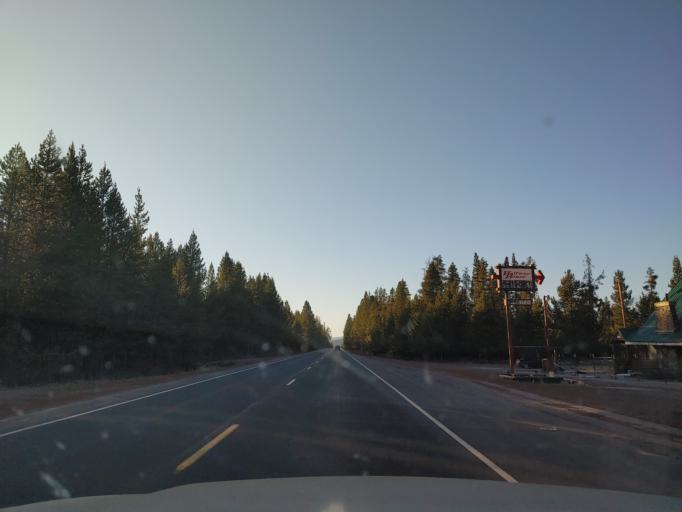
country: US
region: Oregon
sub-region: Deschutes County
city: La Pine
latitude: 43.3884
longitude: -121.8090
